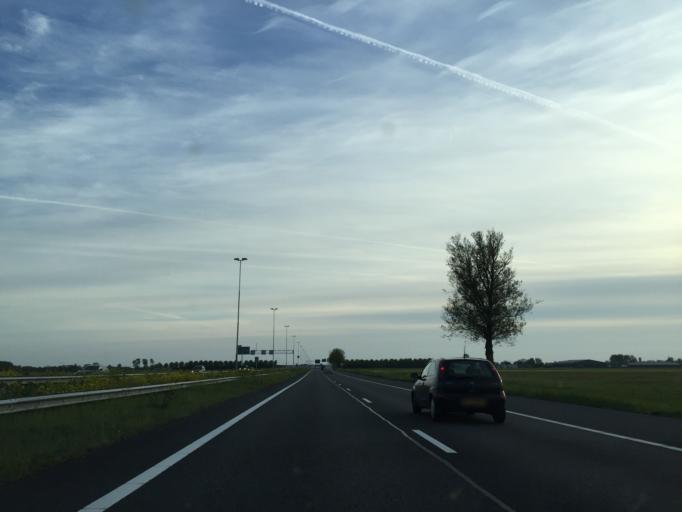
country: NL
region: North Holland
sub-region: Gemeente Beemster
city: Halfweg
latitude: 52.4996
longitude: 4.9103
